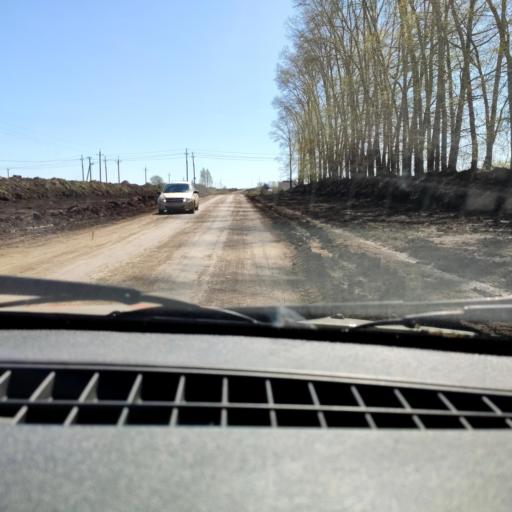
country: RU
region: Bashkortostan
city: Iglino
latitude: 54.8154
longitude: 56.4335
